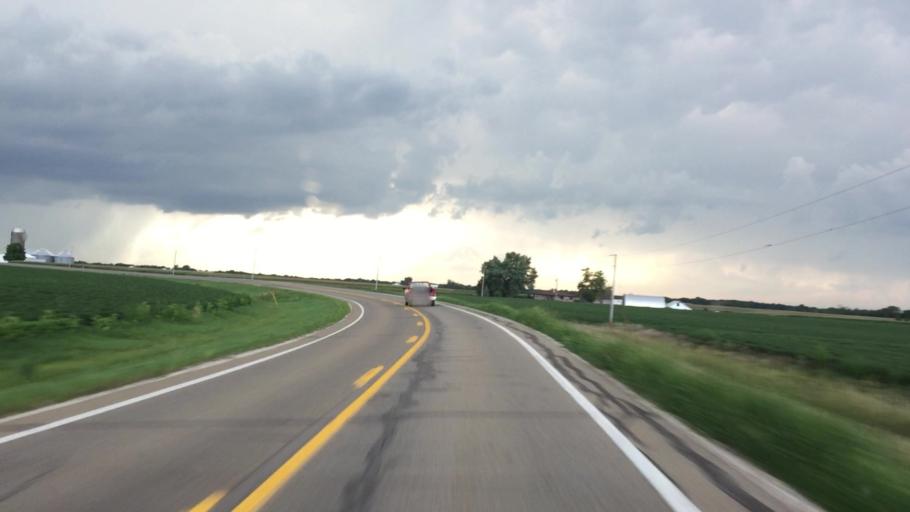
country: US
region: Iowa
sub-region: Henry County
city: New London
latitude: 40.7810
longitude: -91.4778
